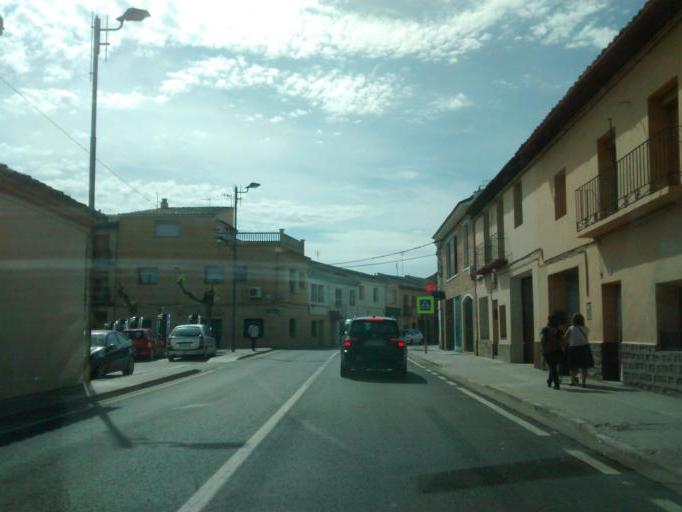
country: ES
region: Aragon
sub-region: Provincia de Zaragoza
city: Quinto
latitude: 41.4241
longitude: -0.4960
